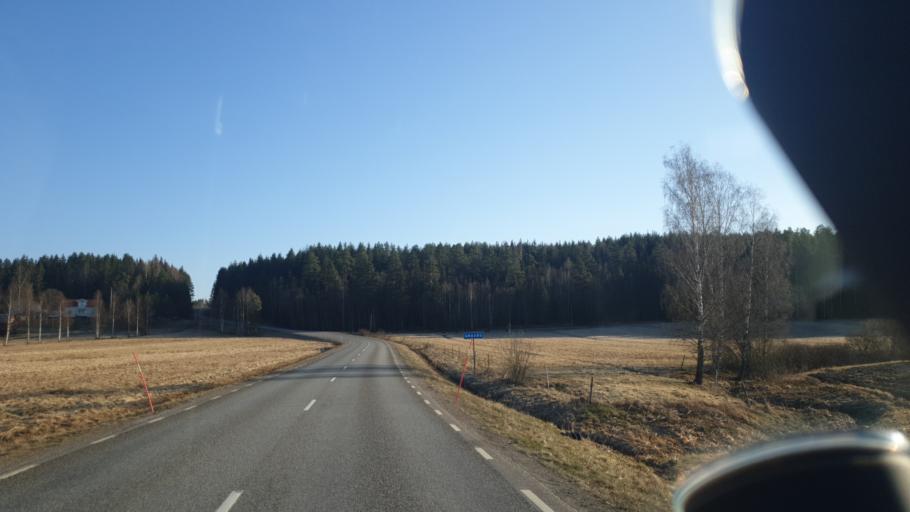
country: SE
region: Vaermland
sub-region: Arvika Kommun
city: Arvika
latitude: 59.7708
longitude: 12.5489
